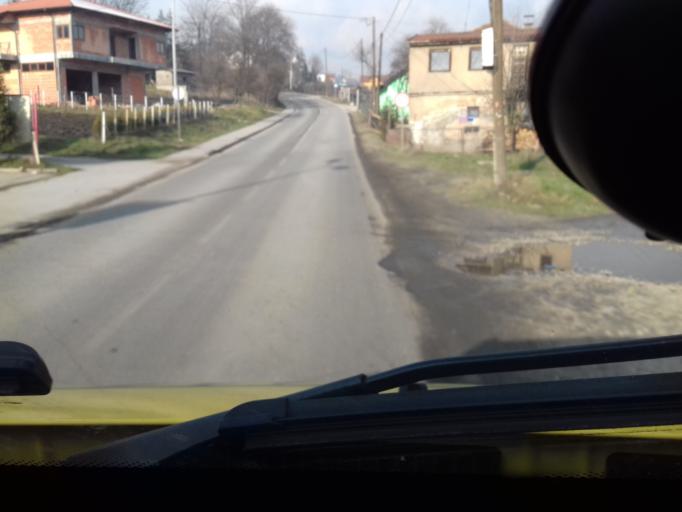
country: BA
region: Federation of Bosnia and Herzegovina
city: Zenica
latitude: 44.2100
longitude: 17.8948
